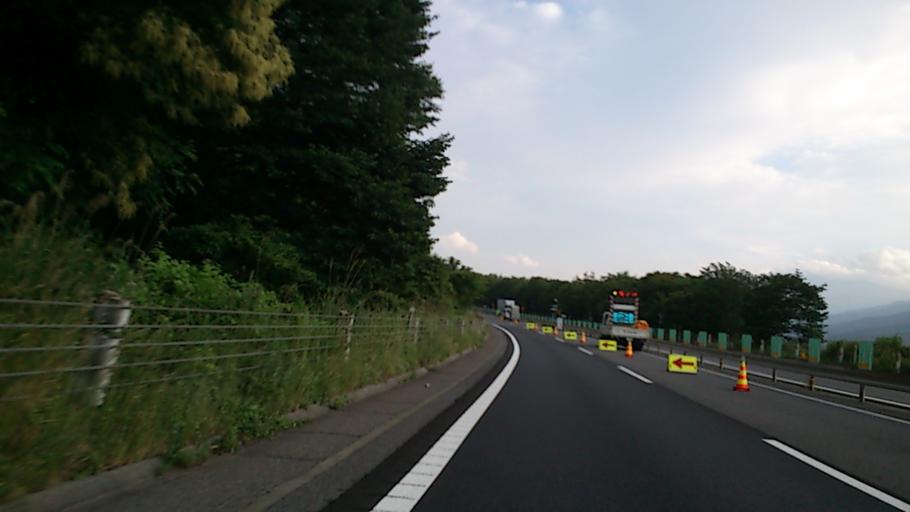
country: JP
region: Nagano
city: Tatsuno
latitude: 35.9903
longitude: 138.0071
